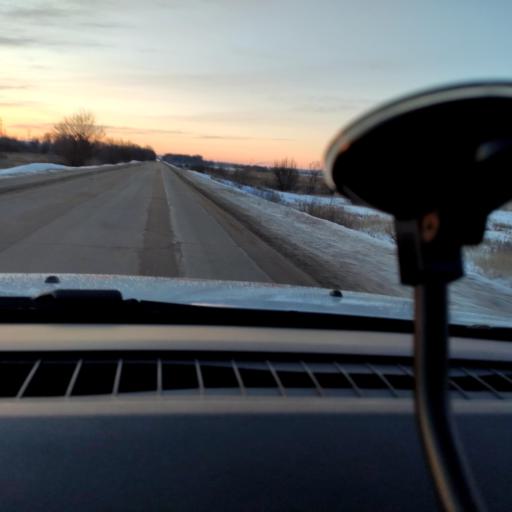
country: RU
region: Samara
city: Samara
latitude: 53.1028
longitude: 50.2277
